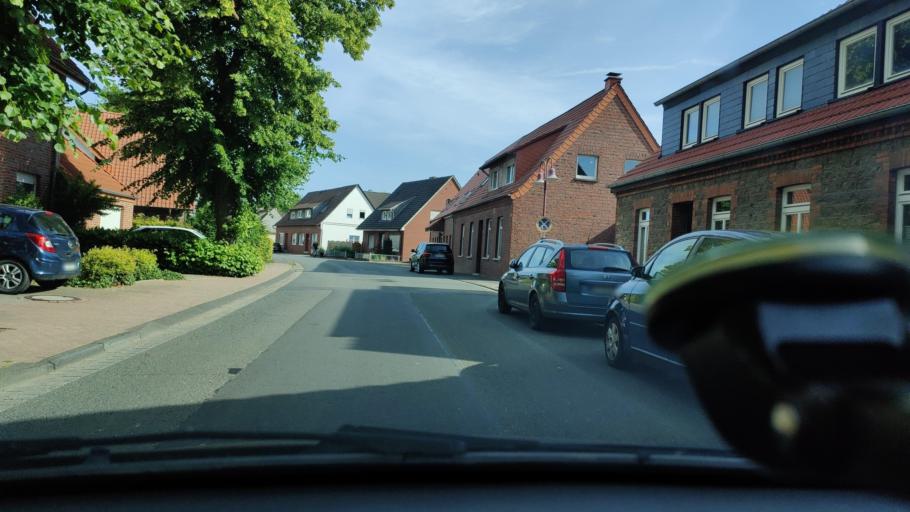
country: DE
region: North Rhine-Westphalia
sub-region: Regierungsbezirk Munster
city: Laer
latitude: 52.0584
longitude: 7.3549
